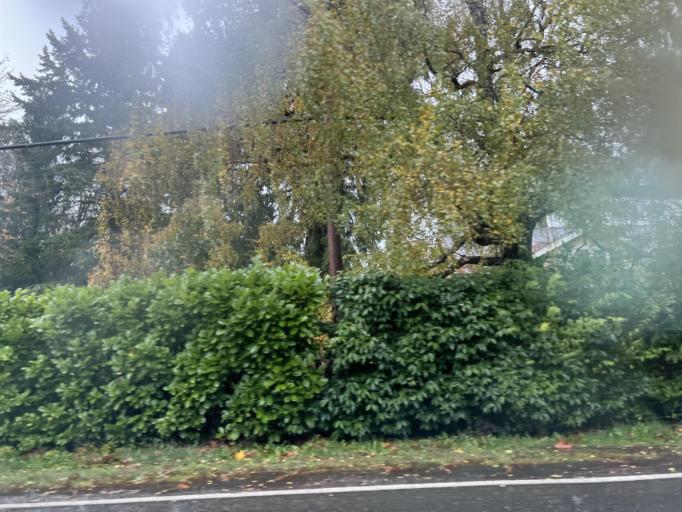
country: US
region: Washington
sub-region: Kitsap County
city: Bainbridge Island
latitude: 47.6558
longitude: -122.5210
